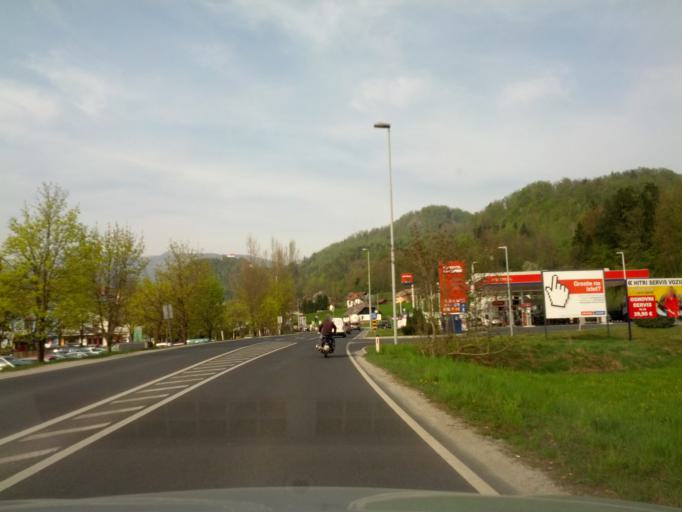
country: SI
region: Kamnik
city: Smarca
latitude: 46.2084
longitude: 14.6059
